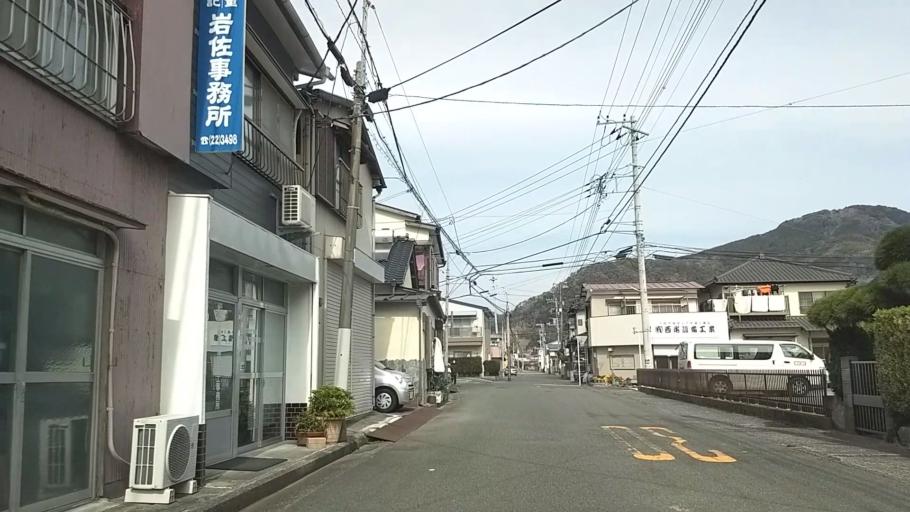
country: JP
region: Shizuoka
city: Shimoda
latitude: 34.6831
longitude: 138.9431
